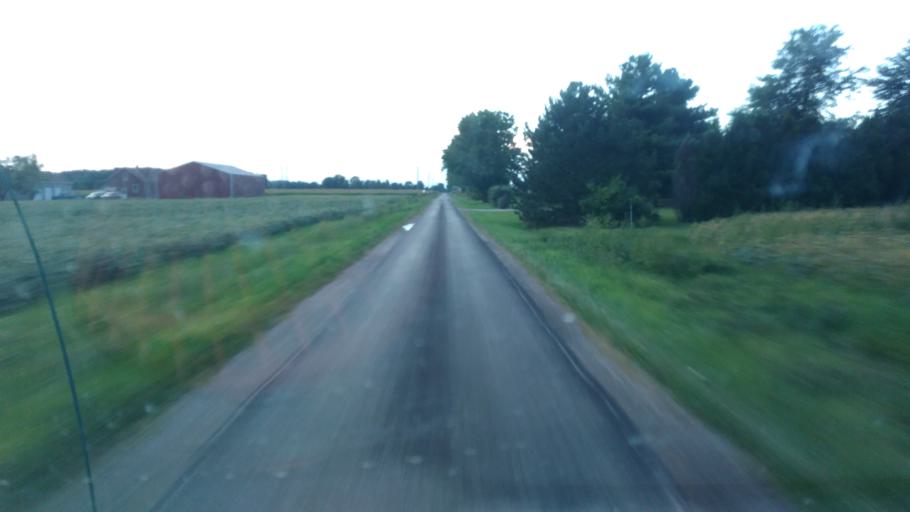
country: US
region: Ohio
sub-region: Crawford County
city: Galion
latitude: 40.7106
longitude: -82.8655
